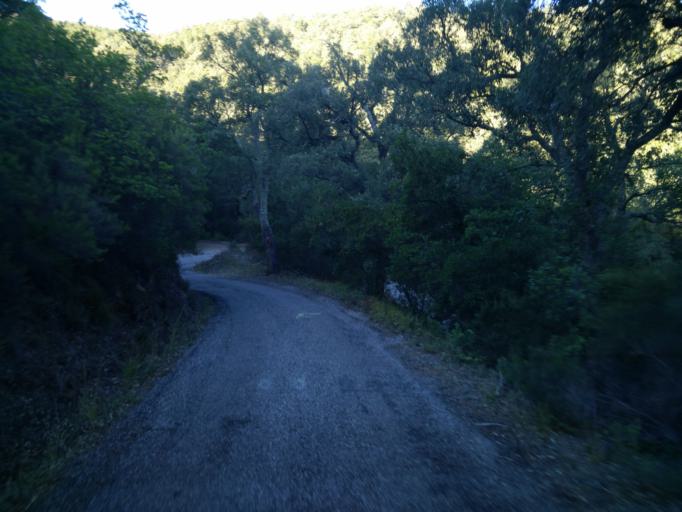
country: FR
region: Provence-Alpes-Cote d'Azur
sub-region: Departement du Var
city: Collobrieres
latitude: 43.2613
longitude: 6.3042
